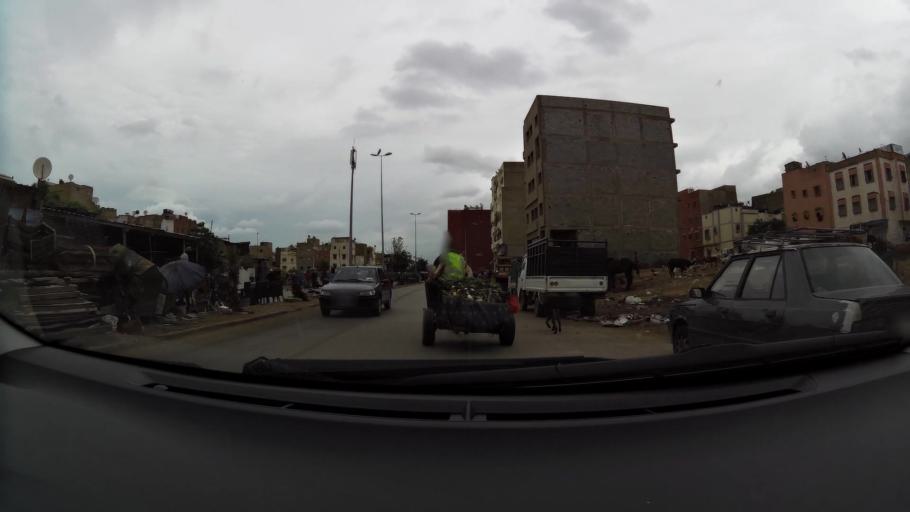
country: MA
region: Grand Casablanca
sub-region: Mediouna
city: Tit Mellil
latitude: 33.5604
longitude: -7.5437
